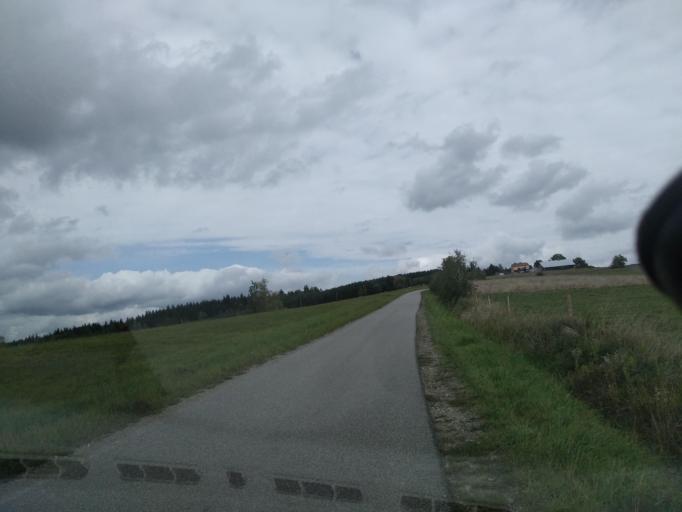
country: PL
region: Lesser Poland Voivodeship
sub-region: Powiat gorlicki
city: Uscie Gorlickie
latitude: 49.5353
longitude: 21.1771
